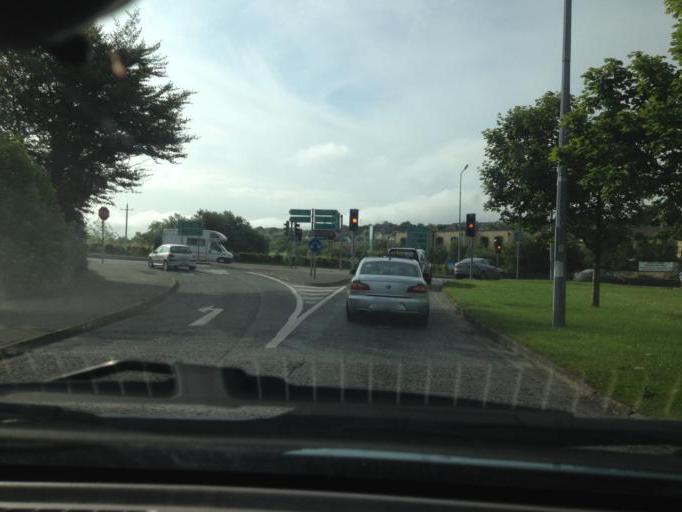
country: IE
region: Connaught
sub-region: Sligo
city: Sligo
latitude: 54.2790
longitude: -8.4746
